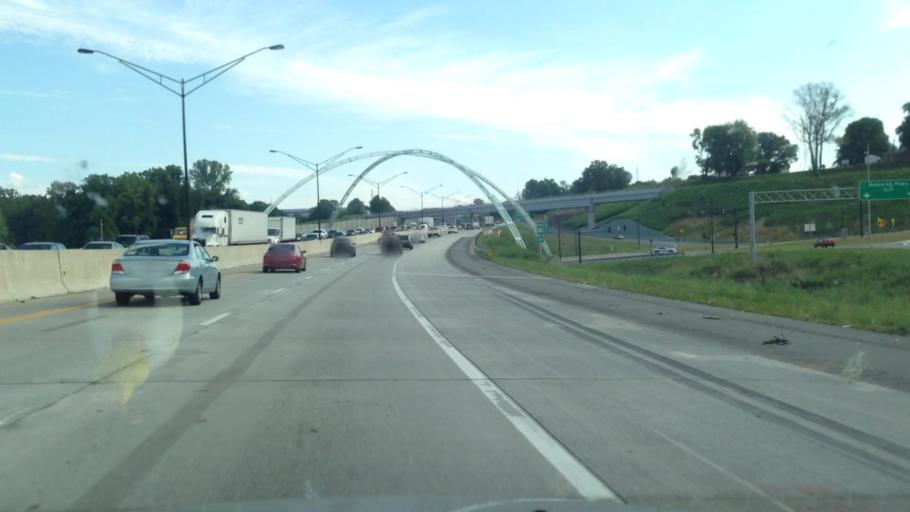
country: US
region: North Carolina
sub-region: Forsyth County
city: Winston-Salem
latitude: 36.0859
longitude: -80.2291
